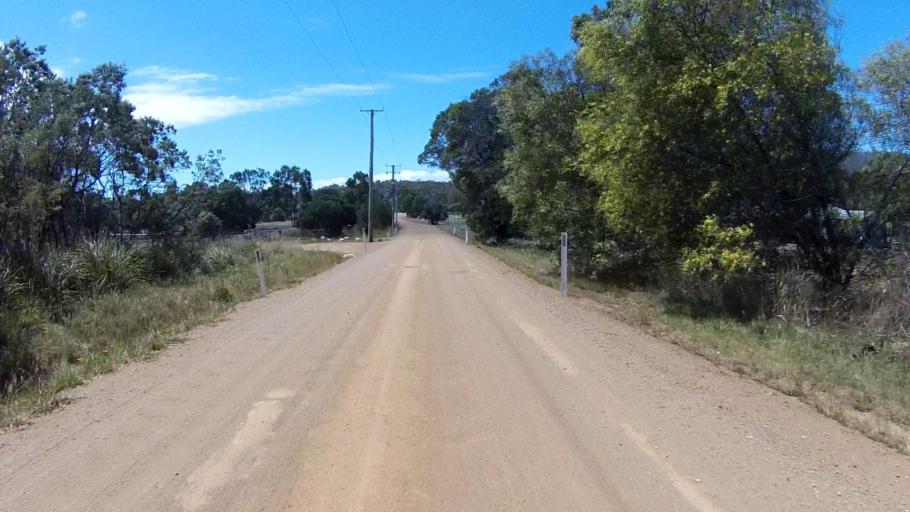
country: AU
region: Tasmania
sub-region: Clarence
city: Sandford
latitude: -42.9656
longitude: 147.4709
